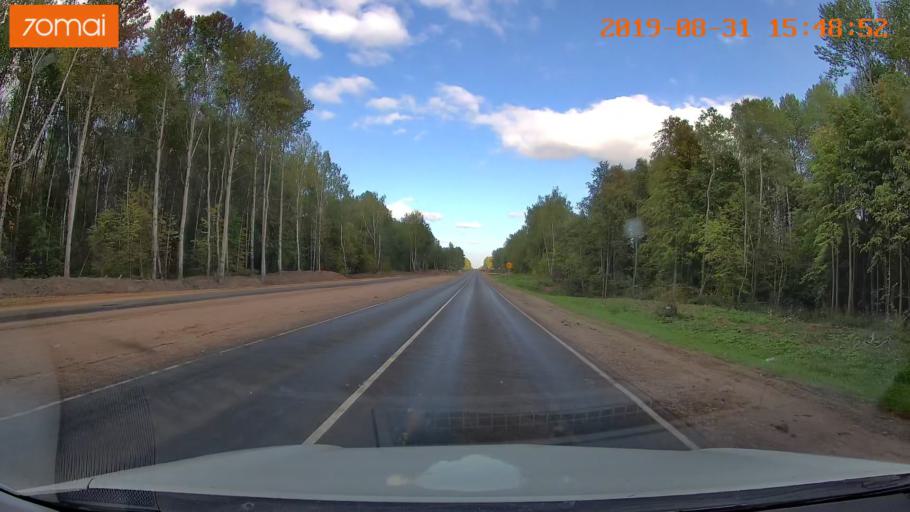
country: RU
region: Kaluga
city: Yukhnov
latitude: 54.6884
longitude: 35.0408
